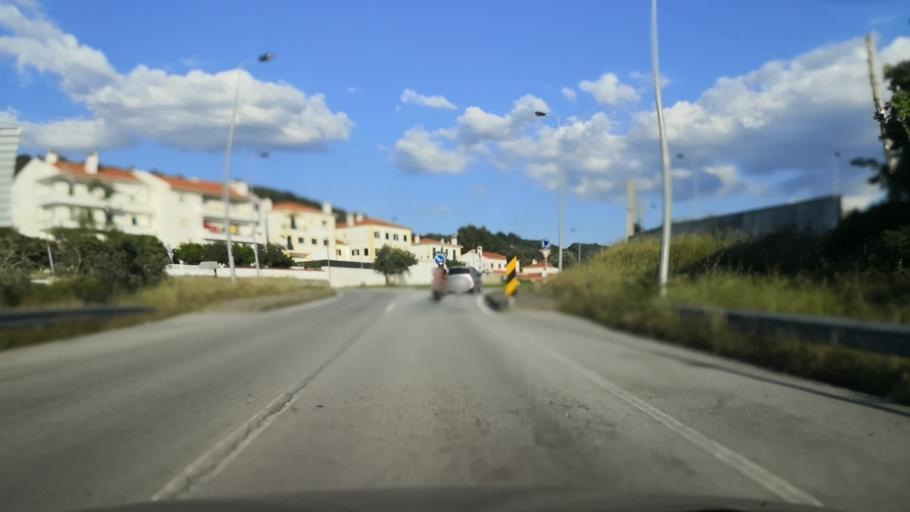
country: PT
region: Portalegre
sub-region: Portalegre
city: Portalegre
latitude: 39.3109
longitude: -7.4416
